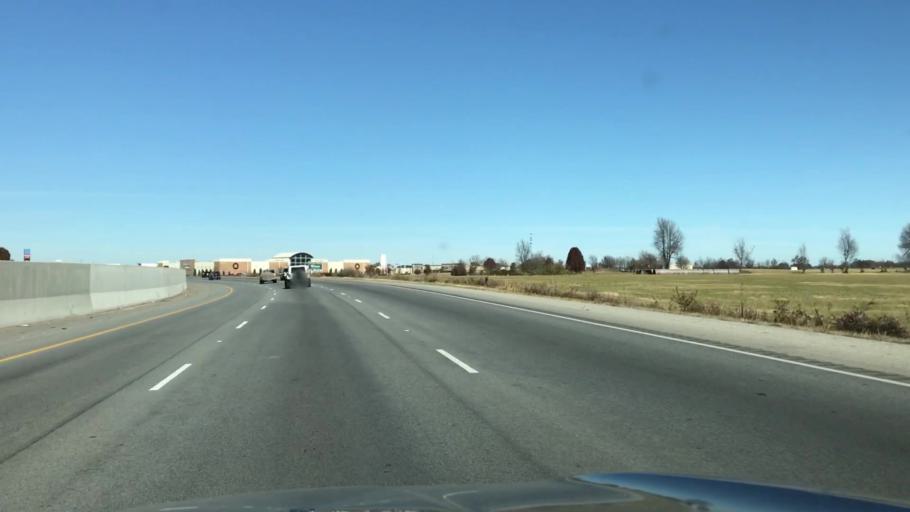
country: US
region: Arkansas
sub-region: Benton County
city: Lowell
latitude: 36.2717
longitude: -94.1513
